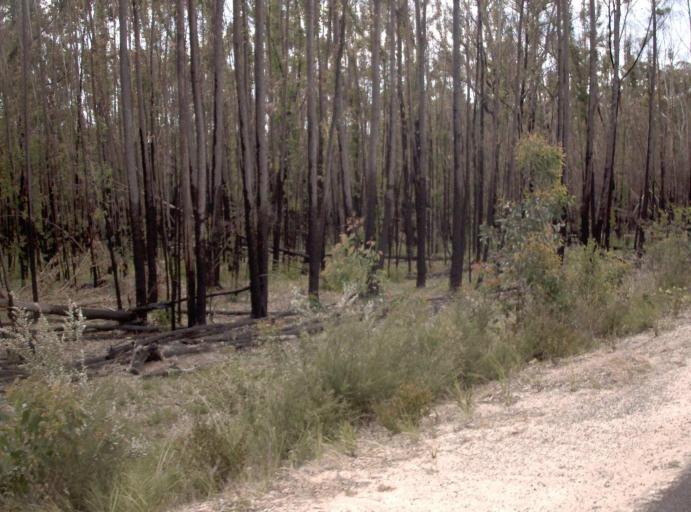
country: AU
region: New South Wales
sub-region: Bega Valley
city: Eden
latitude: -37.5409
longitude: 149.4622
